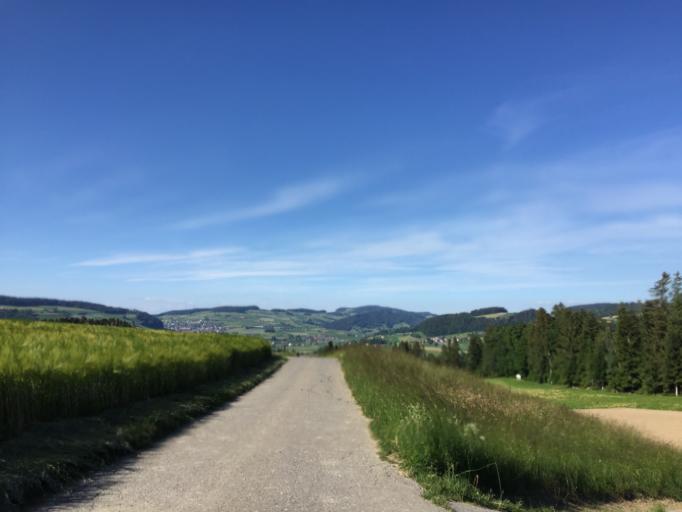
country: CH
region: Lucerne
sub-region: Entlebuch District
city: Oberdiessbach
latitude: 46.8587
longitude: 7.6155
